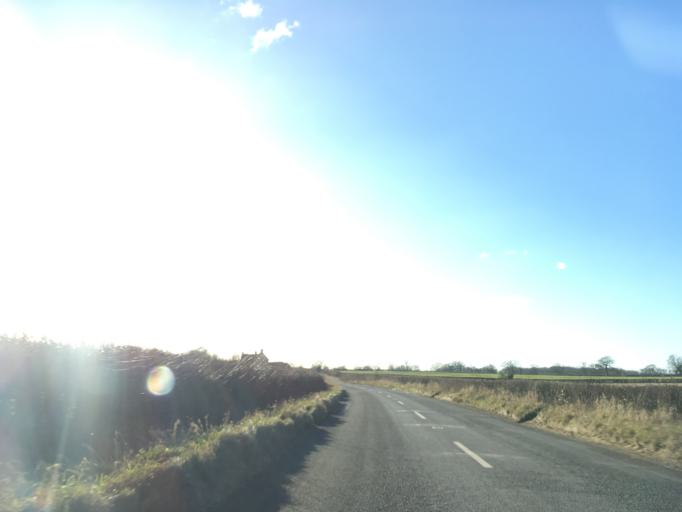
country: GB
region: England
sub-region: Wiltshire
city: Luckington
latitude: 51.5411
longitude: -2.2540
